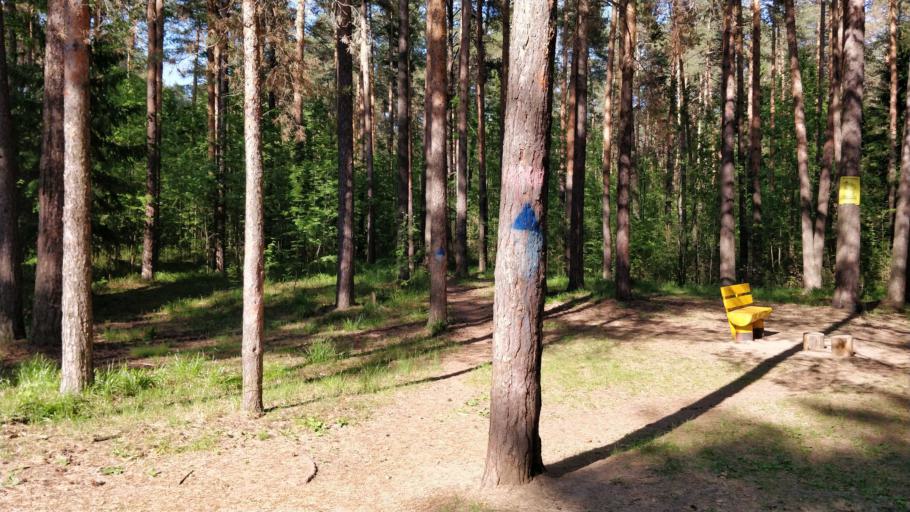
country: RU
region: Perm
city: Kondratovo
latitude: 57.9756
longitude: 56.1380
